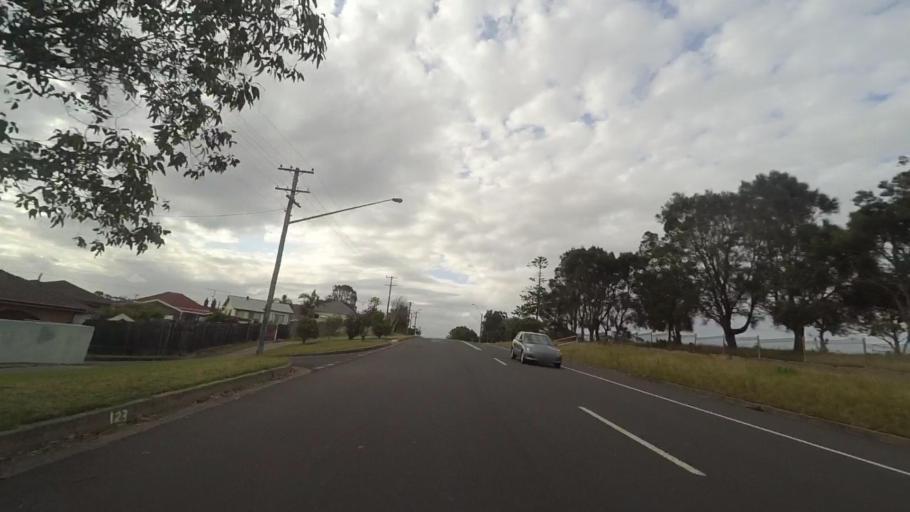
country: AU
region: New South Wales
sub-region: Wollongong
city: Port Kembla
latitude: -34.4847
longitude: 150.9070
